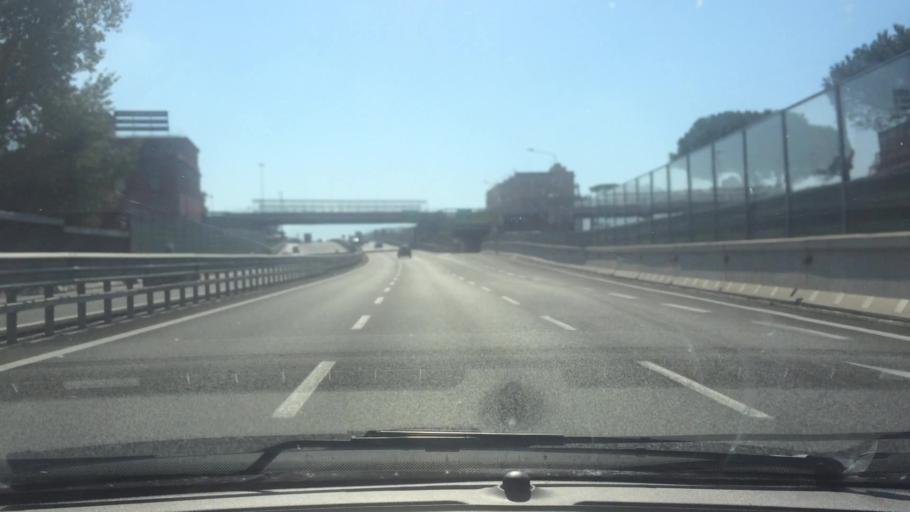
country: IT
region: Campania
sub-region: Provincia di Napoli
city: Ercolano
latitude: 40.8181
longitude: 14.3537
